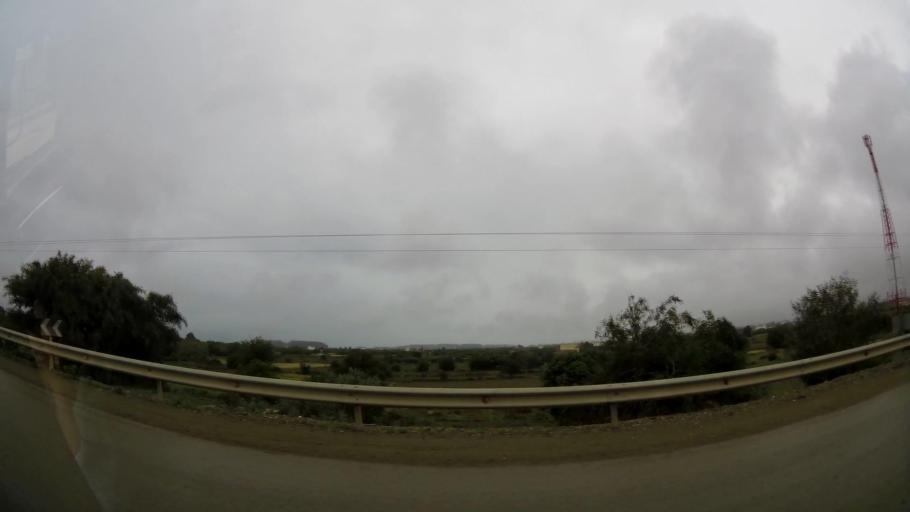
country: MA
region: Taza-Al Hoceima-Taounate
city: Imzourene
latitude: 35.1817
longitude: -3.8792
